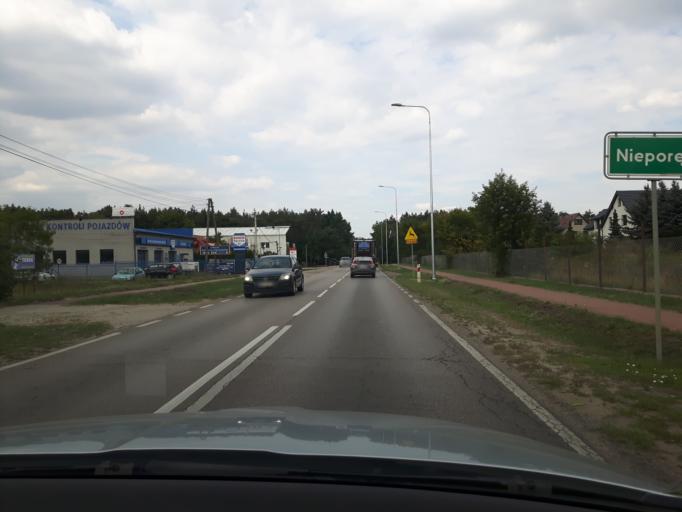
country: PL
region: Masovian Voivodeship
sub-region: Powiat legionowski
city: Stanislawow Pierwszy
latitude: 52.3983
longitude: 21.0357
